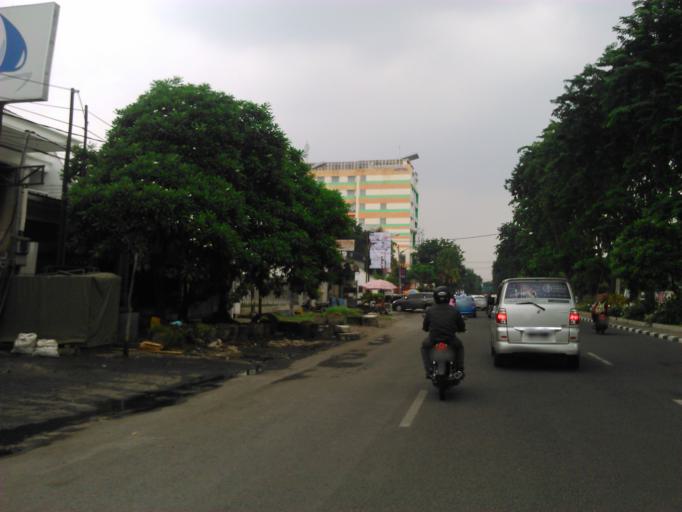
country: ID
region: East Java
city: Gubengairlangga
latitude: -7.2801
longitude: 112.7676
